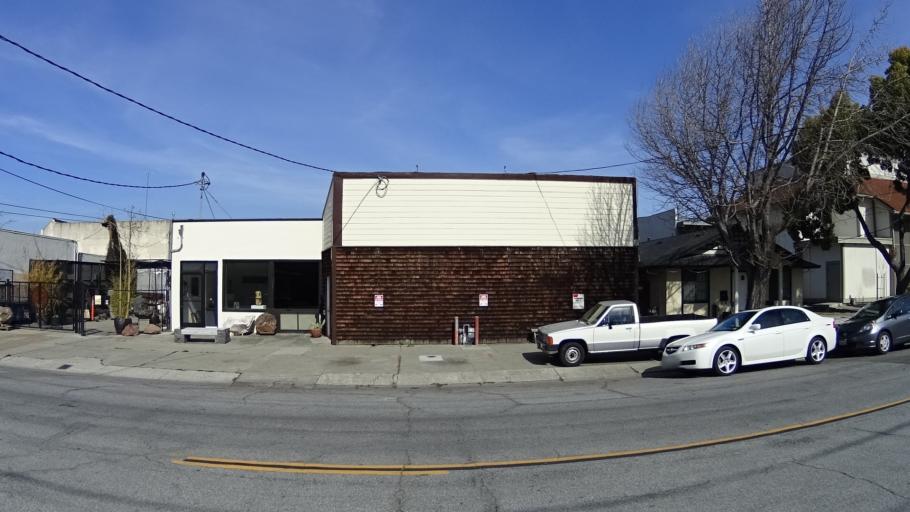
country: US
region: California
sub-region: Santa Clara County
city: San Jose
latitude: 37.3486
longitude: -121.8942
